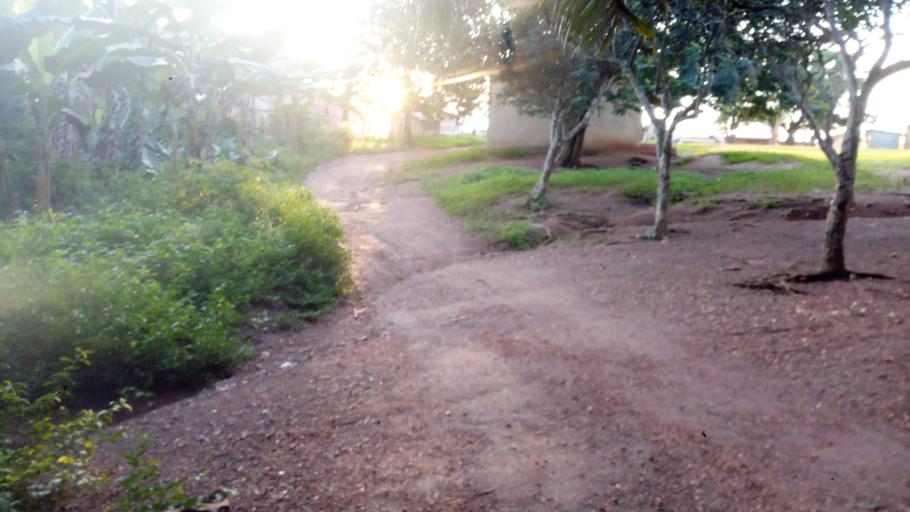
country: GH
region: Eastern
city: Akwatia
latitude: 6.1607
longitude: -0.8164
